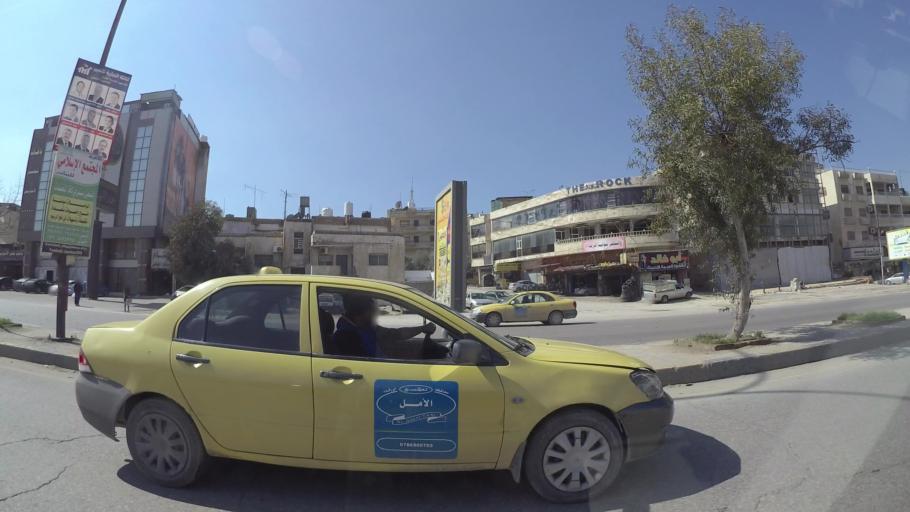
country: JO
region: Zarqa
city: Zarqa
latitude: 32.0342
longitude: 36.0909
